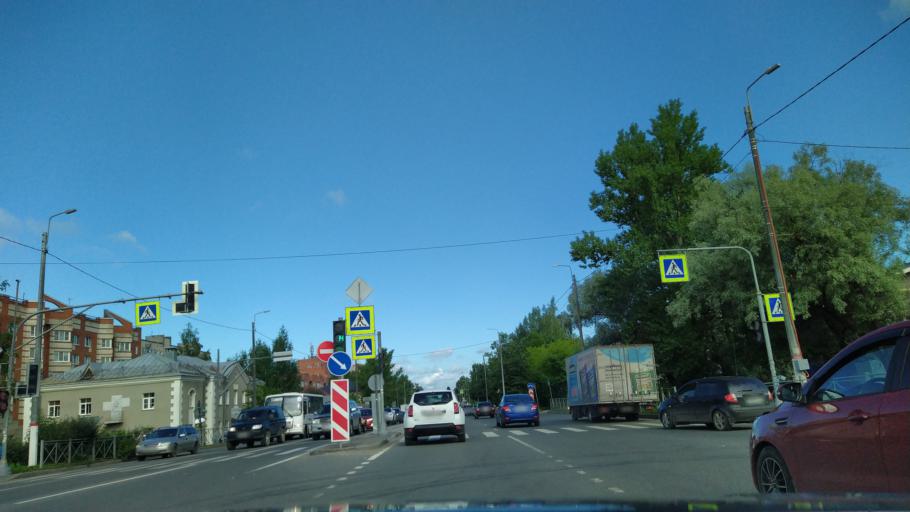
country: RU
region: Leningrad
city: Tosno
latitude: 59.5452
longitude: 30.8695
